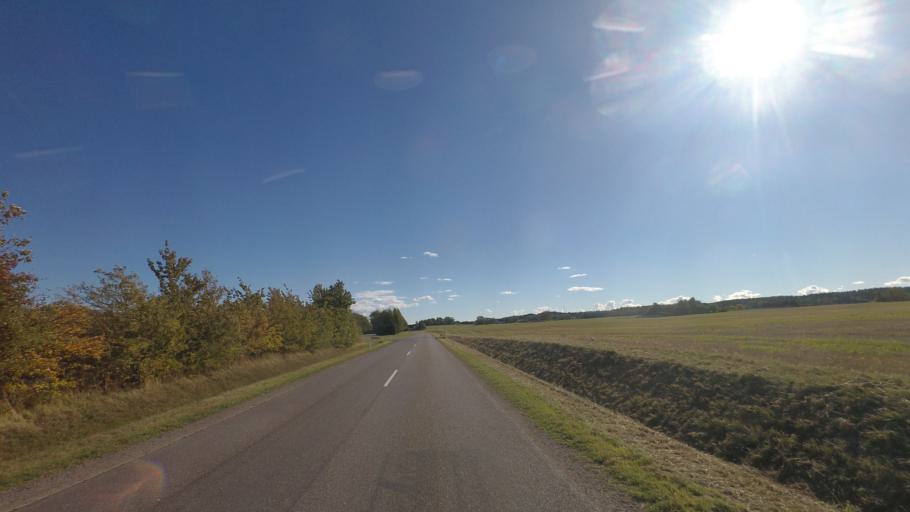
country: DK
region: Capital Region
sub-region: Bornholm Kommune
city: Nexo
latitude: 55.1104
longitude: 15.1108
